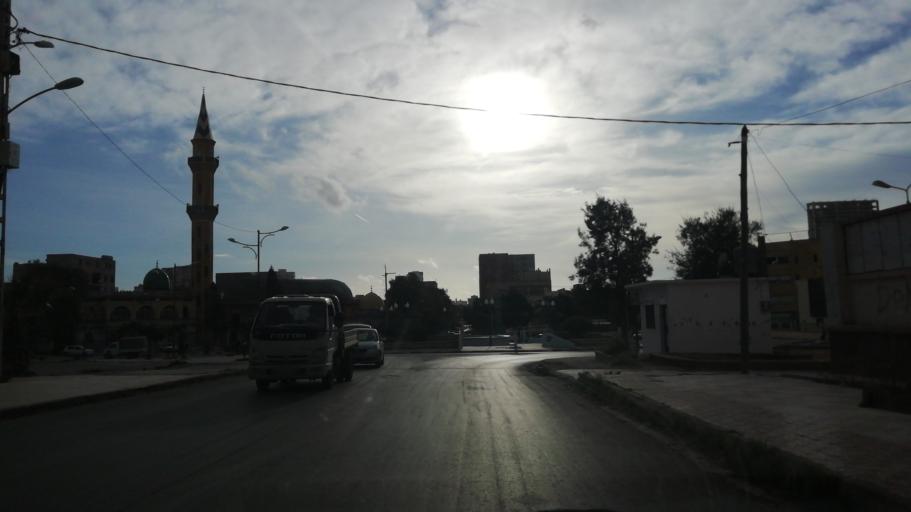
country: DZ
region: Oran
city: Bir el Djir
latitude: 35.7299
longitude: -0.5797
